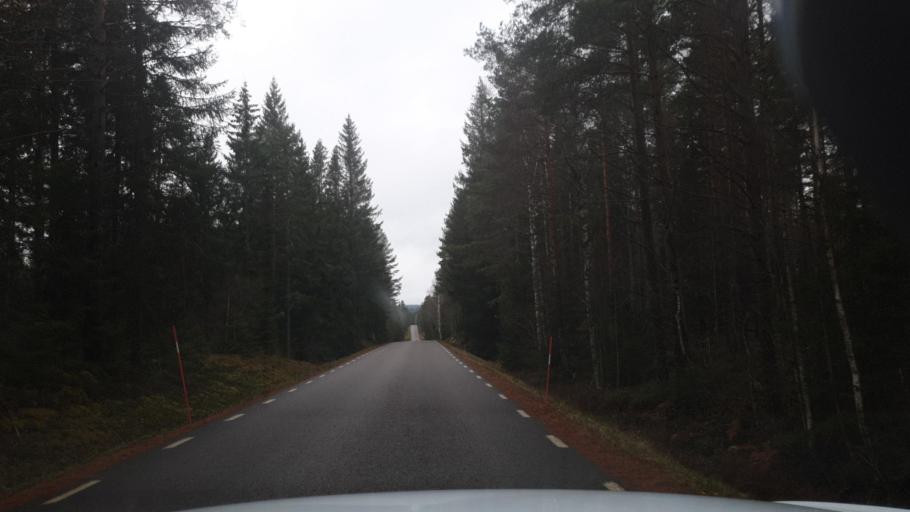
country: SE
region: Vaermland
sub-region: Arvika Kommun
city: Arvika
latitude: 59.5602
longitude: 12.4374
